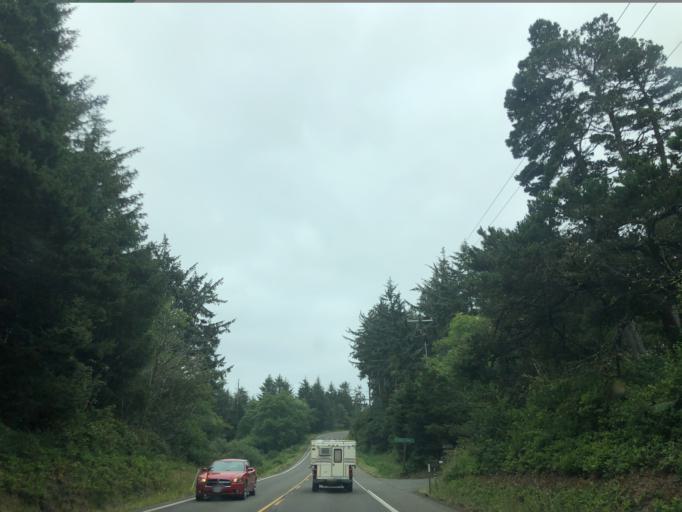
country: US
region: Oregon
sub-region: Lincoln County
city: Waldport
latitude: 44.4808
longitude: -124.0803
